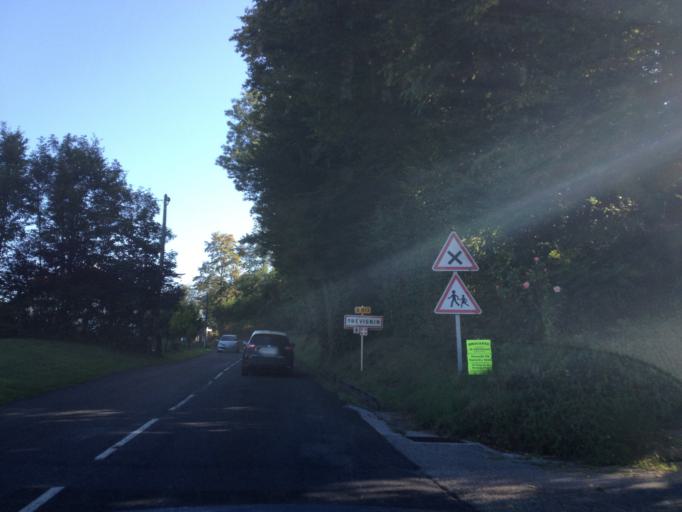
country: FR
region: Rhone-Alpes
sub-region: Departement de la Savoie
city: Gresy-sur-Aix
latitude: 45.7056
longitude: 5.9510
